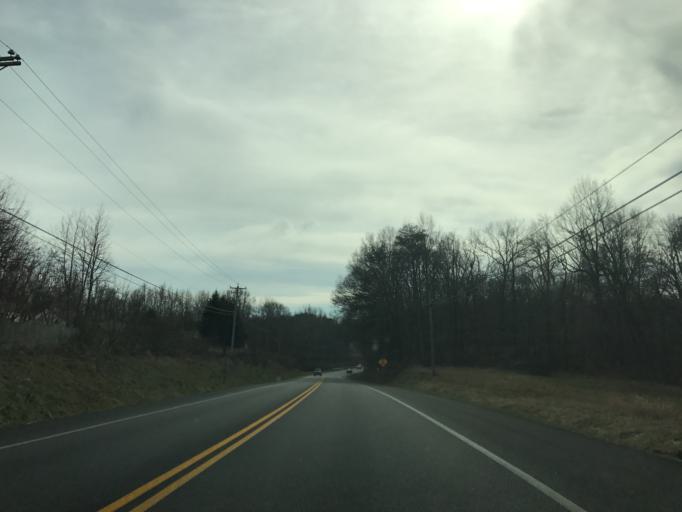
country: US
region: Maryland
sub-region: Queen Anne's County
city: Centreville
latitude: 39.0567
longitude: -76.0539
